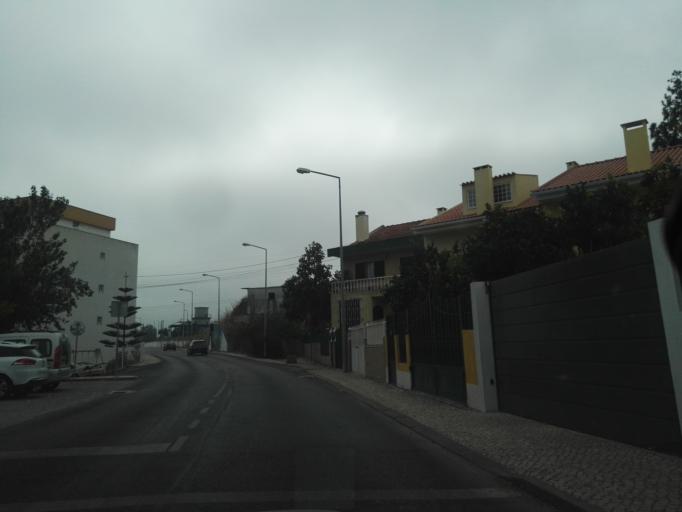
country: PT
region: Lisbon
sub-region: Vila Franca de Xira
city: Sobralinho
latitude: 38.9054
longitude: -9.0375
